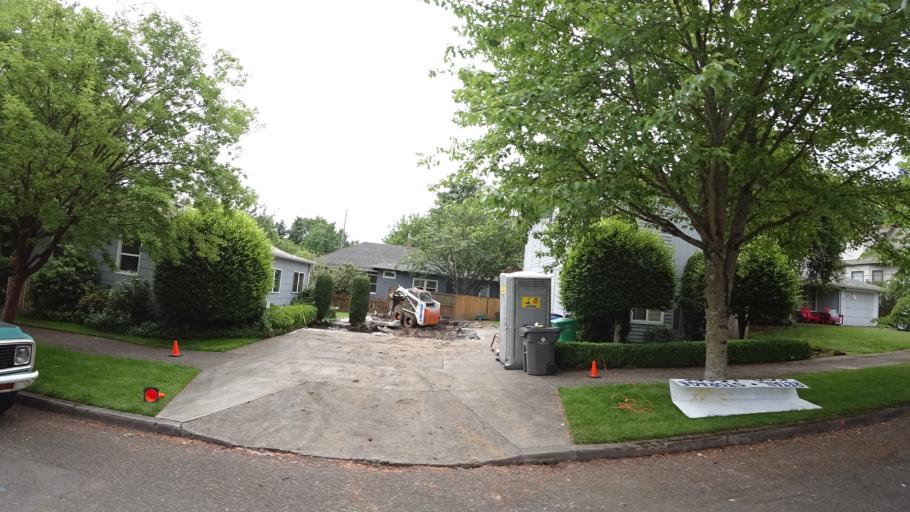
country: US
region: Oregon
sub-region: Clackamas County
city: Milwaukie
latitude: 45.4758
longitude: -122.6743
